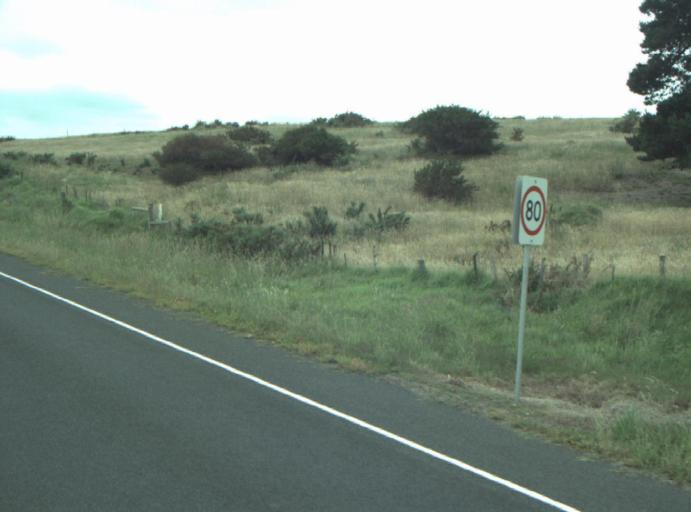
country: AU
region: Victoria
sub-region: Queenscliffe
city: Queenscliff
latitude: -38.2614
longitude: 144.5635
